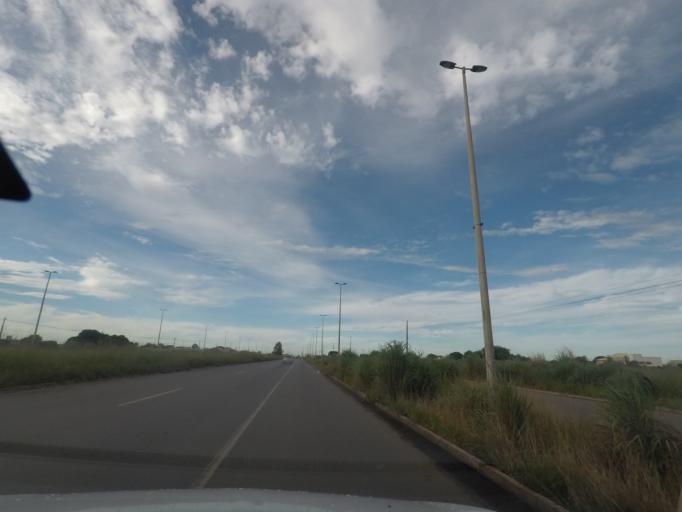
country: BR
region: Goias
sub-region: Aparecida De Goiania
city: Aparecida de Goiania
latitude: -16.7740
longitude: -49.3520
